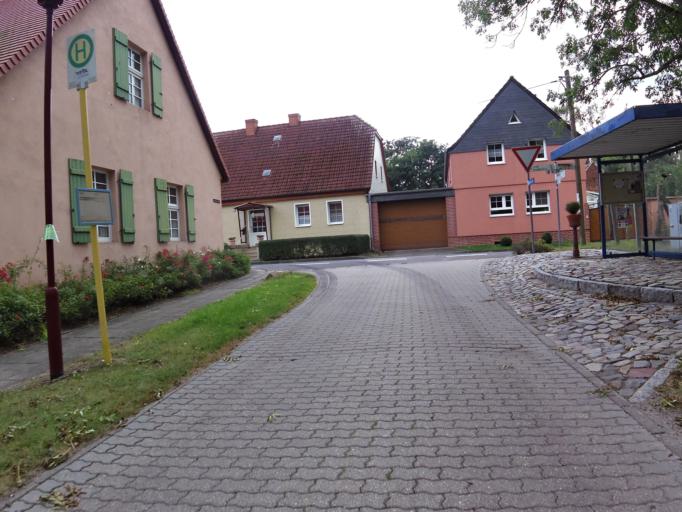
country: DE
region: Saxony-Anhalt
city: Gross Rosenburg
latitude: 51.9346
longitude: 11.9529
